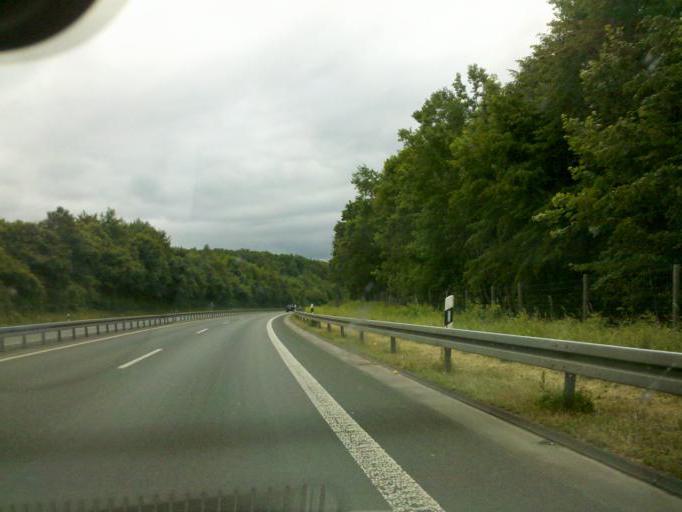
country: DE
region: North Rhine-Westphalia
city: Kreuztal
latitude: 50.9462
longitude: 8.0033
